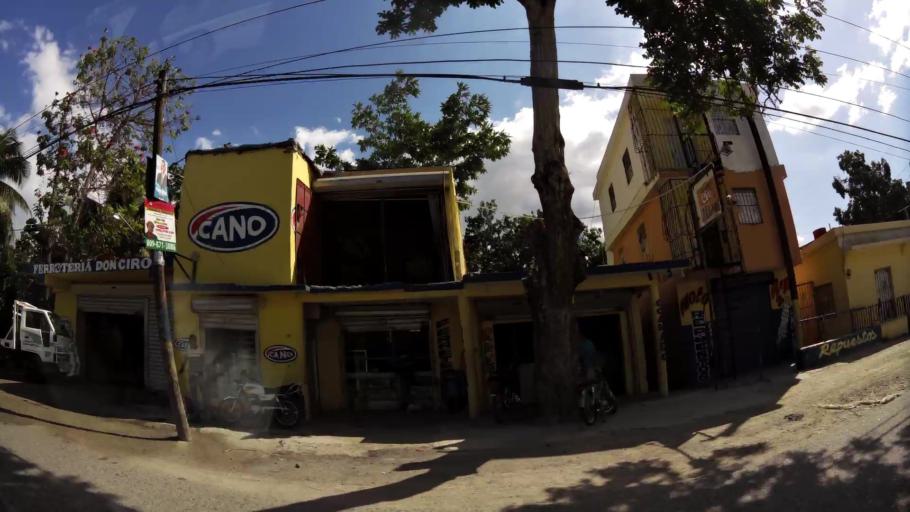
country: DO
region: San Cristobal
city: San Cristobal
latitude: 18.4248
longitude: -70.0707
